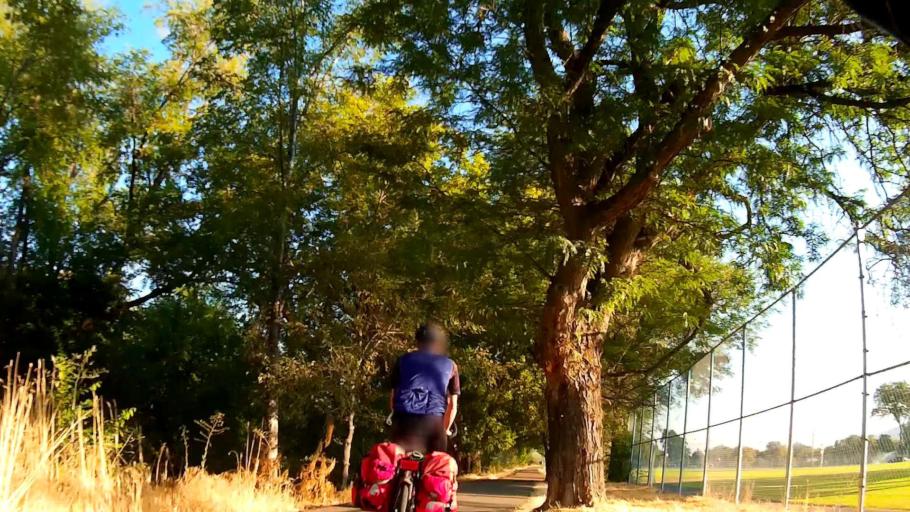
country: US
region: Utah
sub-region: Salt Lake County
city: Salt Lake City
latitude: 40.7825
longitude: -111.9360
